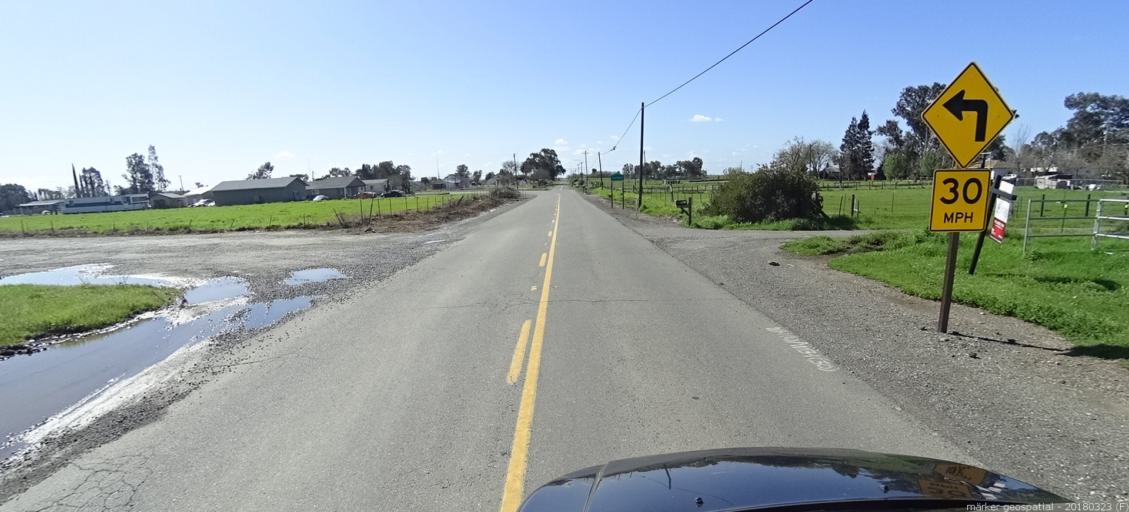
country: US
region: California
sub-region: Sacramento County
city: Elverta
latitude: 38.7342
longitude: -121.4844
